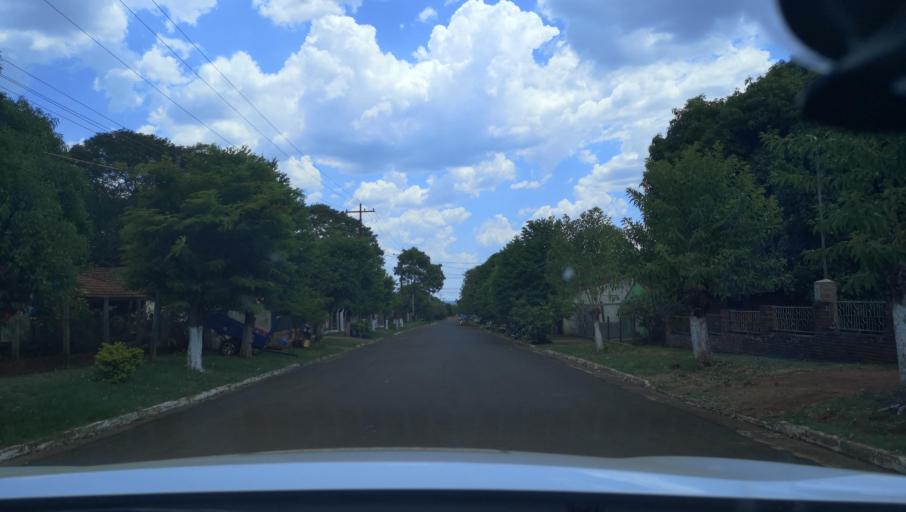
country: PY
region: Itapua
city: Carmen del Parana
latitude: -27.1694
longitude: -56.2335
